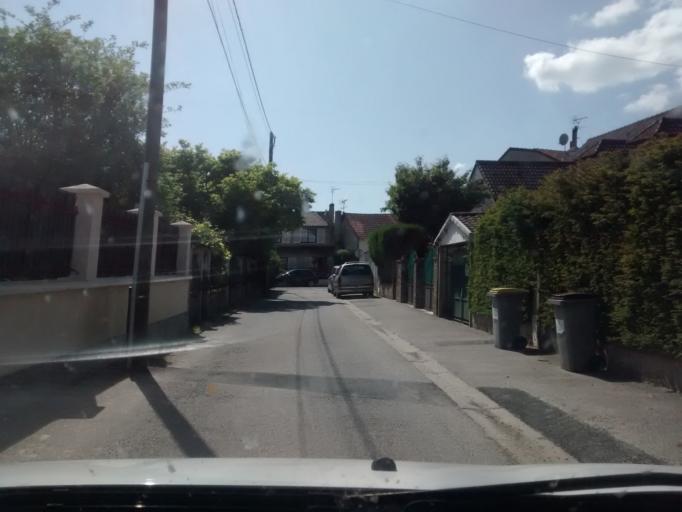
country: FR
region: Ile-de-France
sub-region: Departement des Yvelines
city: Trappes
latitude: 48.7735
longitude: 1.9974
